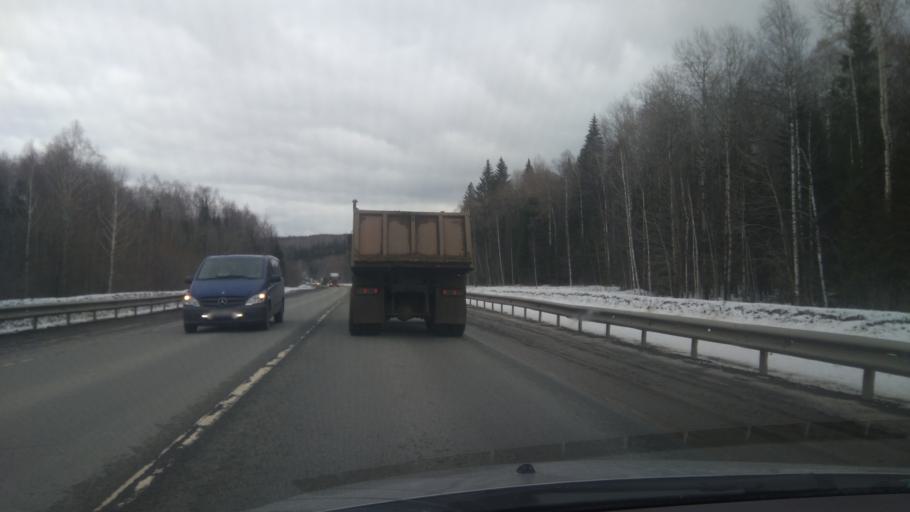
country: RU
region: Sverdlovsk
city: Bisert'
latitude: 56.8285
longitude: 59.0968
